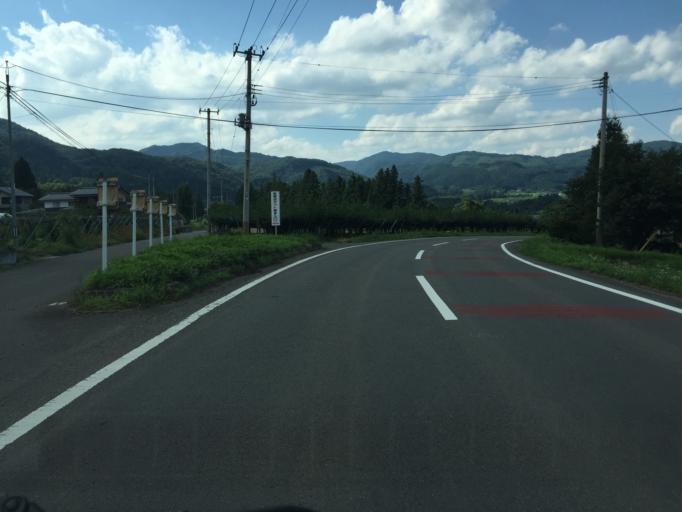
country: JP
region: Fukushima
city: Fukushima-shi
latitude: 37.7585
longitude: 140.3611
